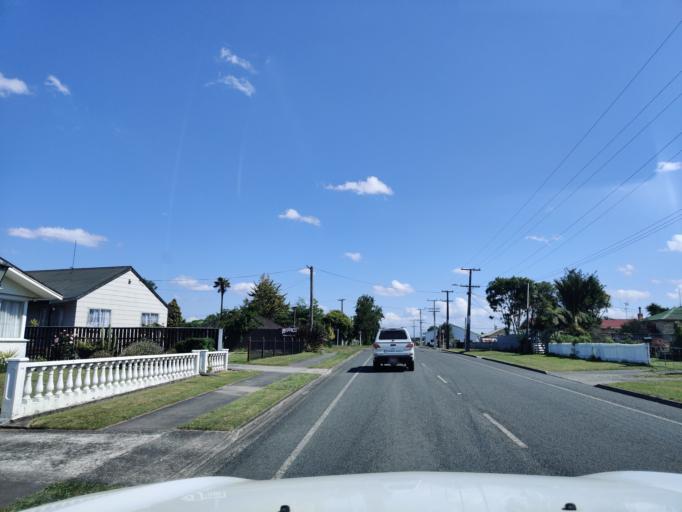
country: NZ
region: Waikato
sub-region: Waikato District
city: Ngaruawahia
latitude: -37.6618
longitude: 175.1434
